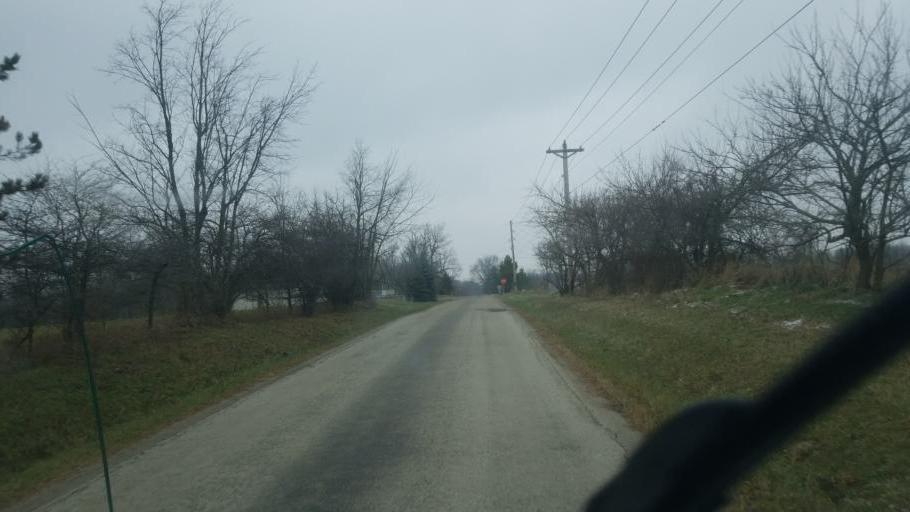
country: US
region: Ohio
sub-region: Huron County
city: New London
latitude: 41.0571
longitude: -82.3265
